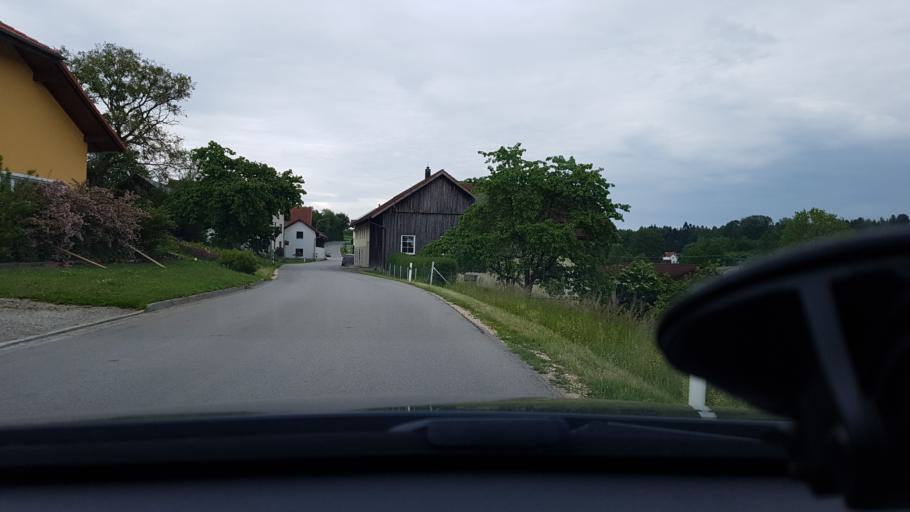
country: DE
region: Bavaria
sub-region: Lower Bavaria
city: Wittibreut
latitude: 48.3427
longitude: 13.0360
